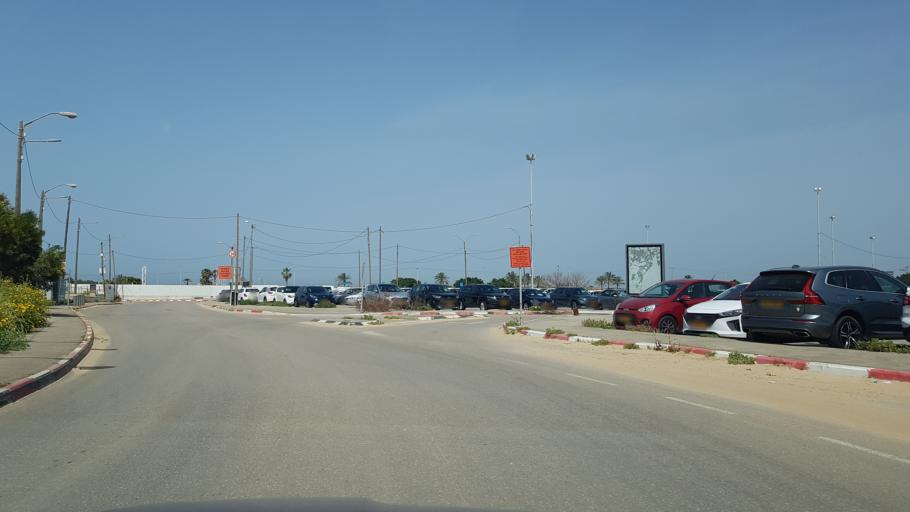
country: IL
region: Tel Aviv
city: Herzliyya
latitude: 32.1470
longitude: 34.8068
